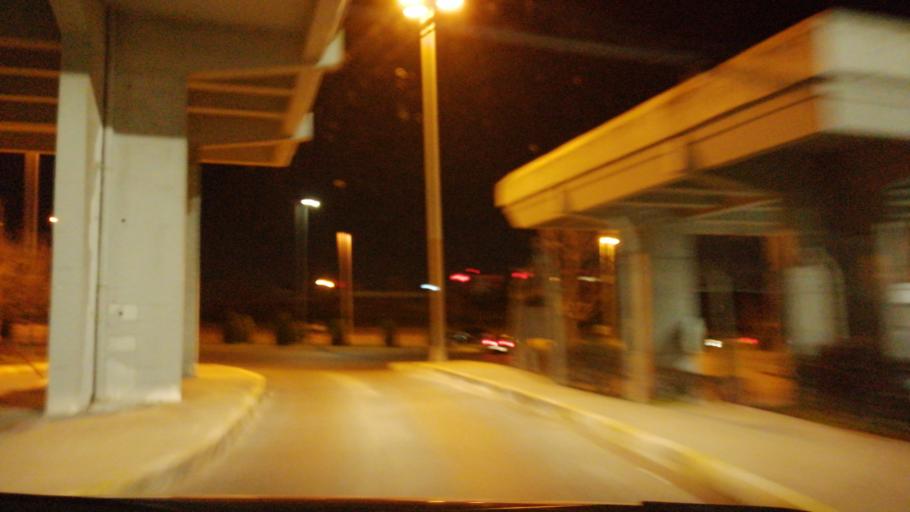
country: TR
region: Istanbul
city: Bahcelievler
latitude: 40.9808
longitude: 28.8259
